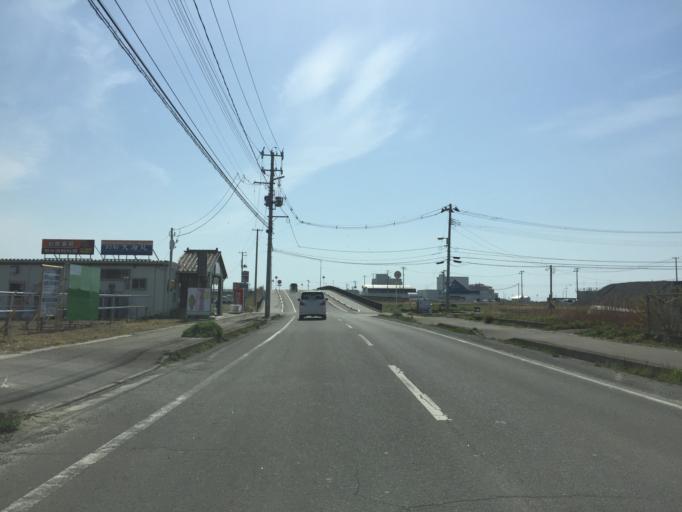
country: JP
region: Miyagi
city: Watari
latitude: 38.0412
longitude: 140.9113
